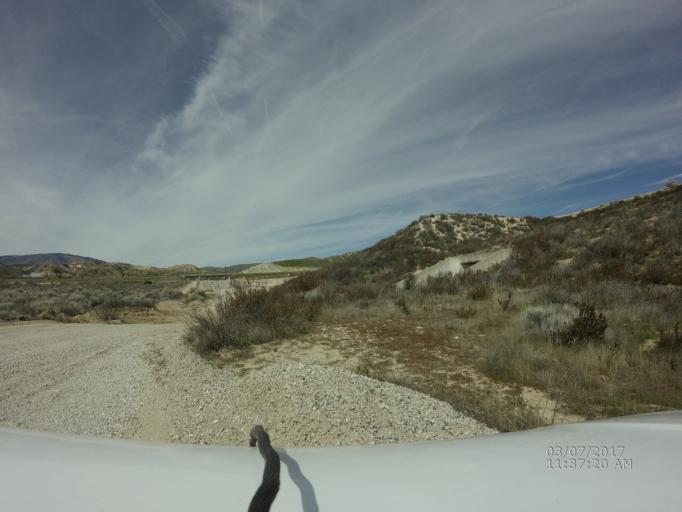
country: US
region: California
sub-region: Kern County
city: Lebec
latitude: 34.7597
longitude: -118.7904
